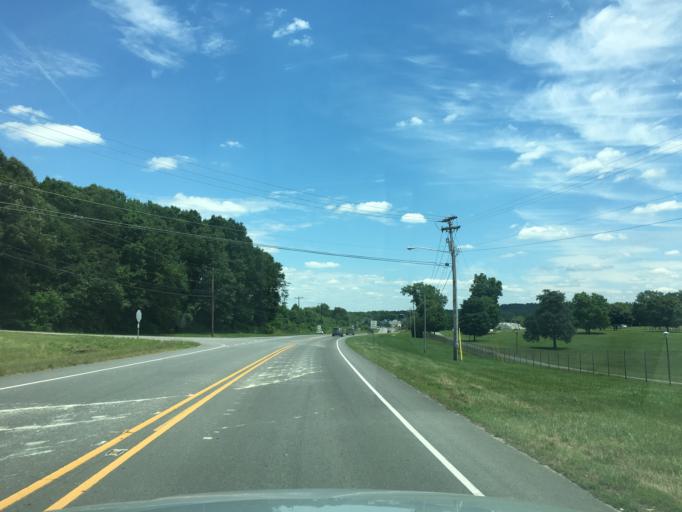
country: US
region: North Carolina
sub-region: Burke County
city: Morganton
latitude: 35.7478
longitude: -81.7200
